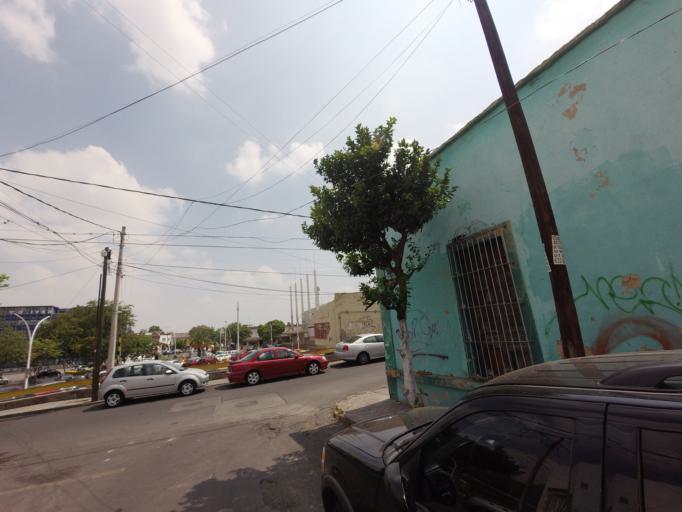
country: MX
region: Jalisco
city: Guadalajara
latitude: 20.6802
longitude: -103.3384
